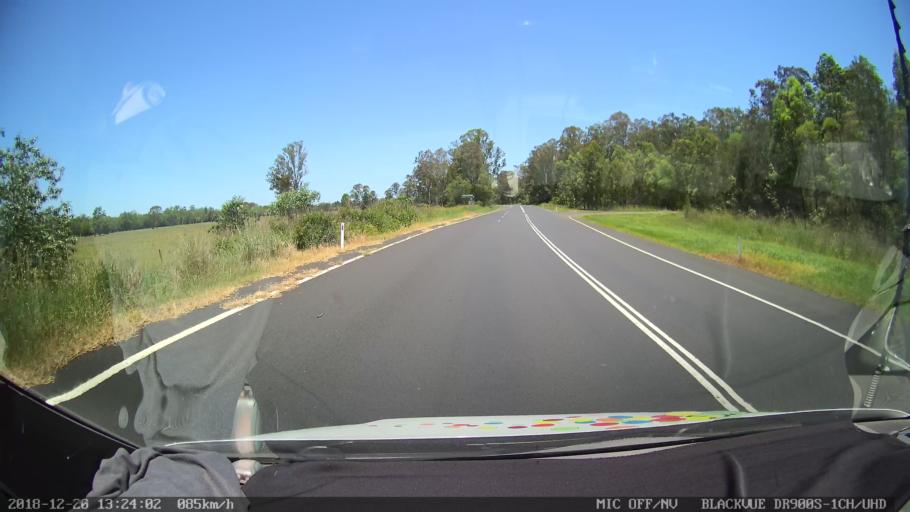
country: AU
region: New South Wales
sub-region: Richmond Valley
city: Casino
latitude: -29.1121
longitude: 153.0006
